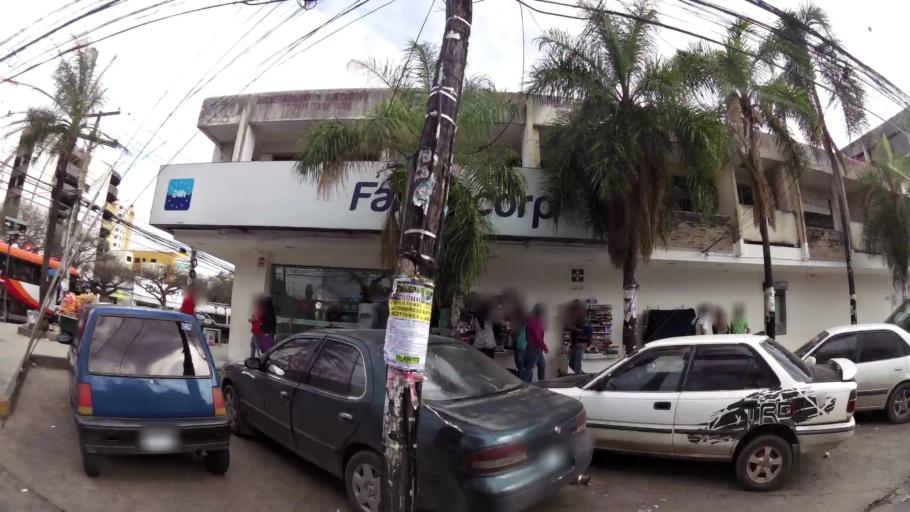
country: BO
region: Santa Cruz
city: Santa Cruz de la Sierra
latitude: -17.7783
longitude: -63.1887
